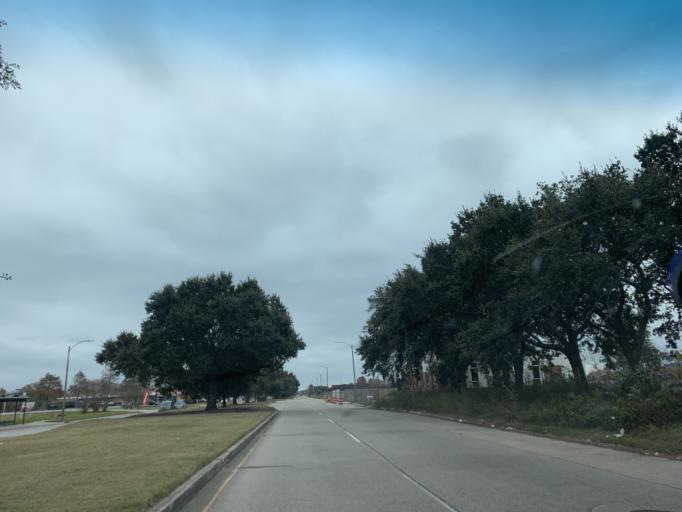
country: US
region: Louisiana
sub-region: Saint Bernard Parish
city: Arabi
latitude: 30.0436
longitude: -89.9591
